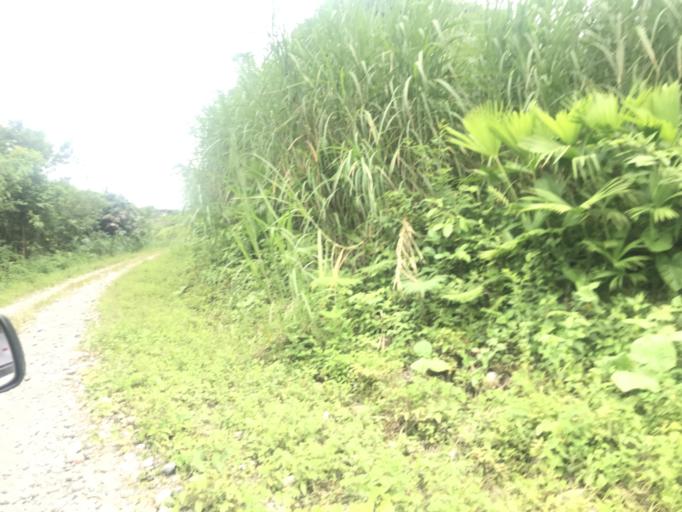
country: EC
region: Napo
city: Tena
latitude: -1.0211
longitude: -77.7423
